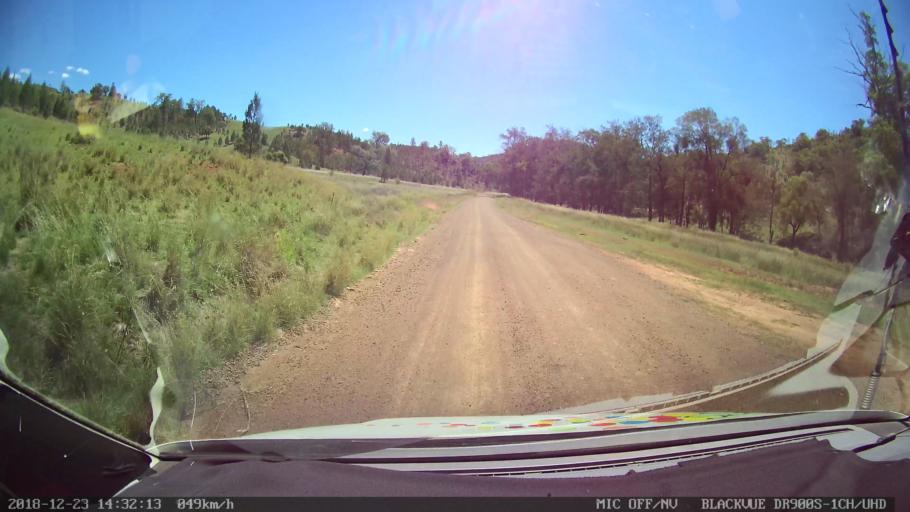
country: AU
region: New South Wales
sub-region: Tamworth Municipality
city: Manilla
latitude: -30.6038
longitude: 150.9204
